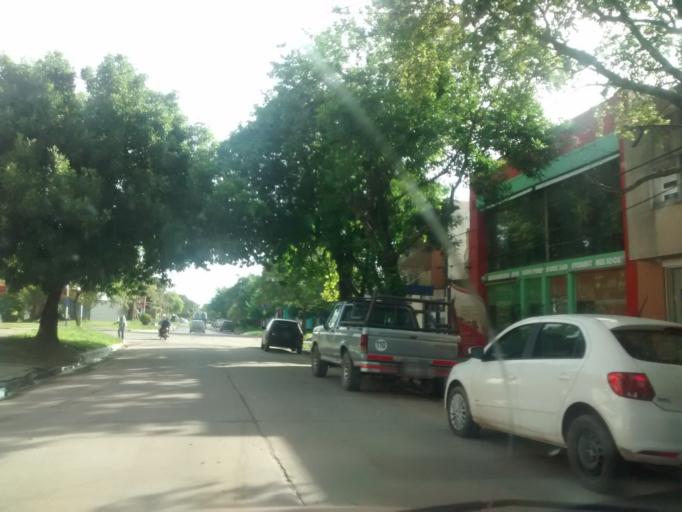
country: AR
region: Chaco
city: Resistencia
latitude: -27.4499
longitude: -58.9747
